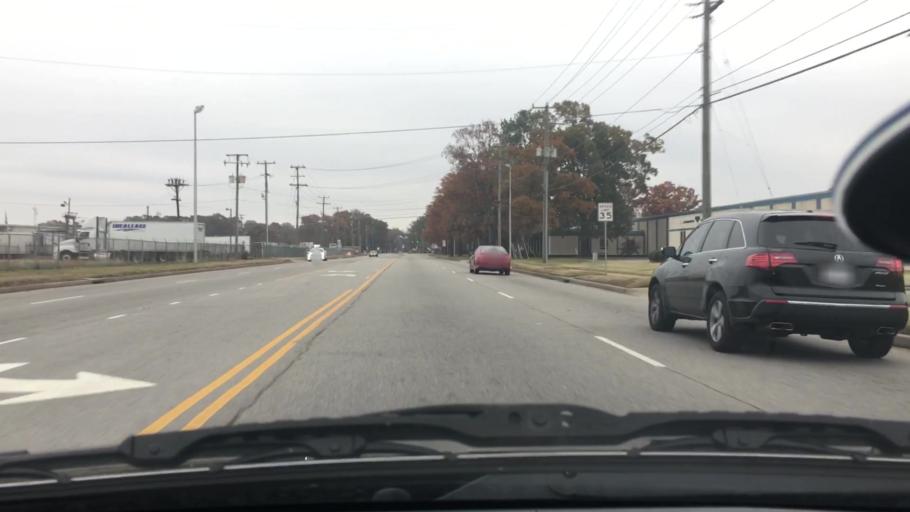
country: US
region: Virginia
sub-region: City of Norfolk
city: Norfolk
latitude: 36.8582
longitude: -76.2420
